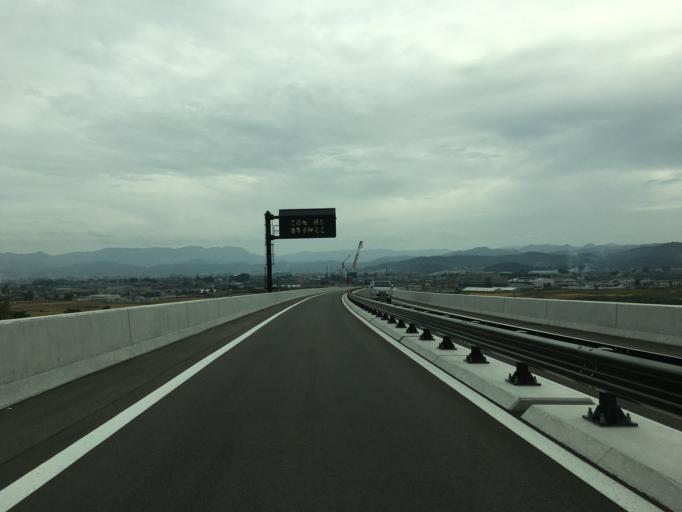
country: JP
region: Fukushima
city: Hobaramachi
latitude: 37.8317
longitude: 140.5039
